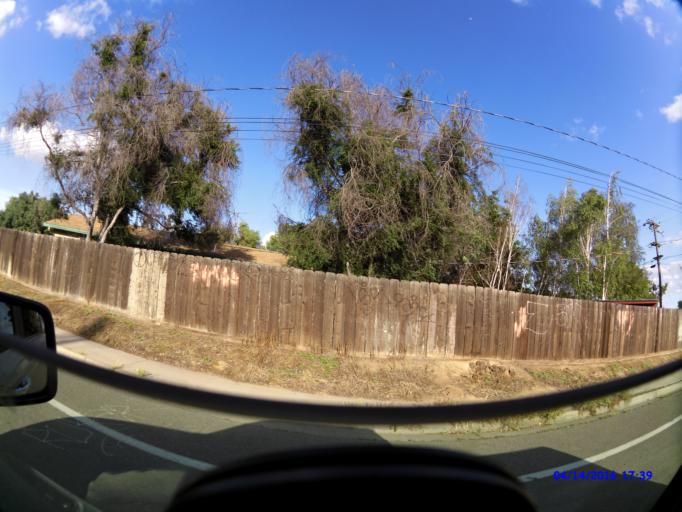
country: US
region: California
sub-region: Stanislaus County
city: Bystrom
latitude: 37.6495
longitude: -120.9573
